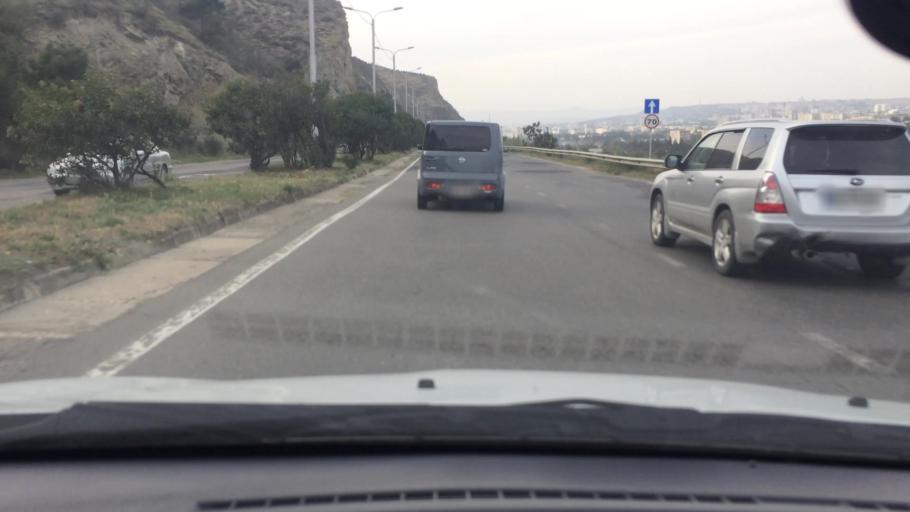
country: GE
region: T'bilisi
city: Tbilisi
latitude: 41.6527
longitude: 44.9025
